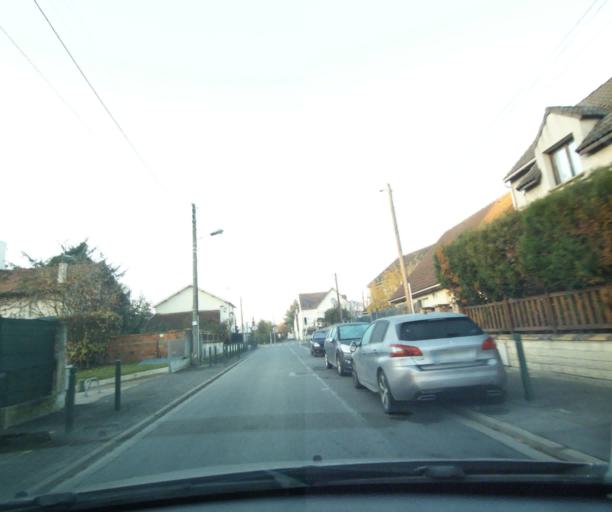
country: FR
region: Ile-de-France
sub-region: Departement de Seine-Saint-Denis
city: Gagny
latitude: 48.8691
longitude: 2.5294
